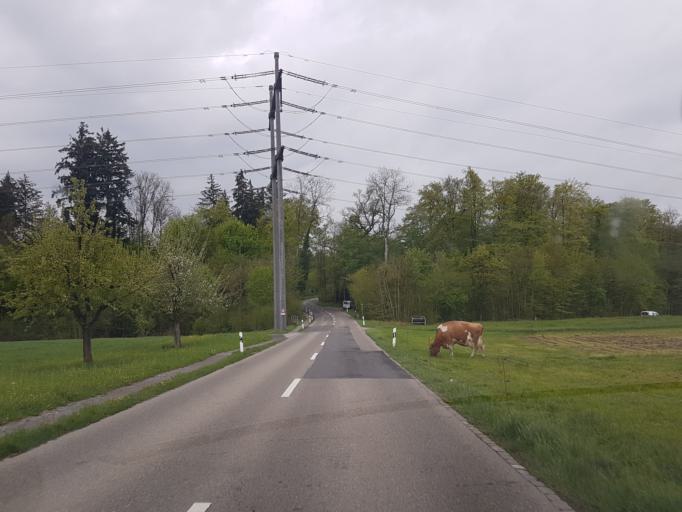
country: CH
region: Zurich
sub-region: Bezirk Dietikon
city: Uitikon
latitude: 47.3666
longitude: 8.4468
